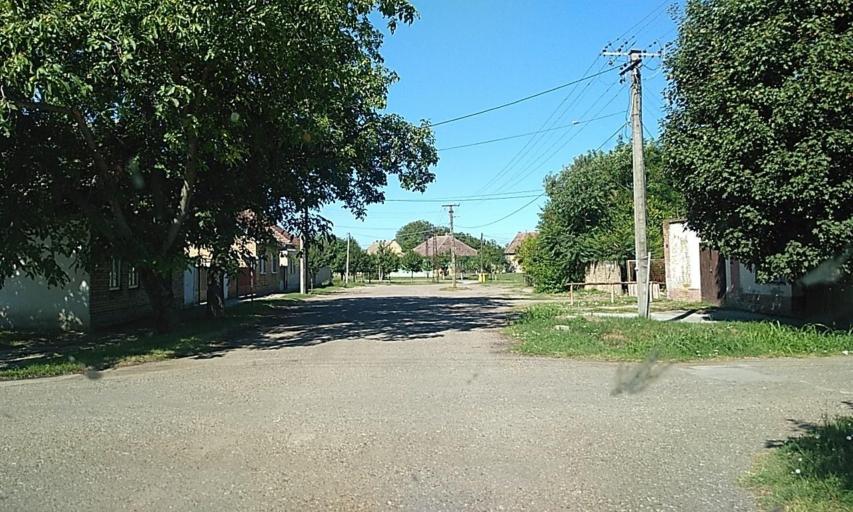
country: RS
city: Backo Gradiste
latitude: 45.5372
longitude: 20.0348
